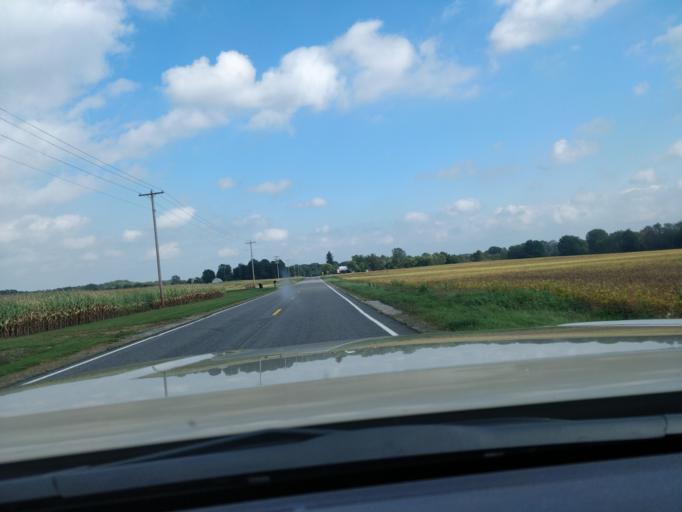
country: US
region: Michigan
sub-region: Ionia County
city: Saranac
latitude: 42.8861
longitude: -85.2221
